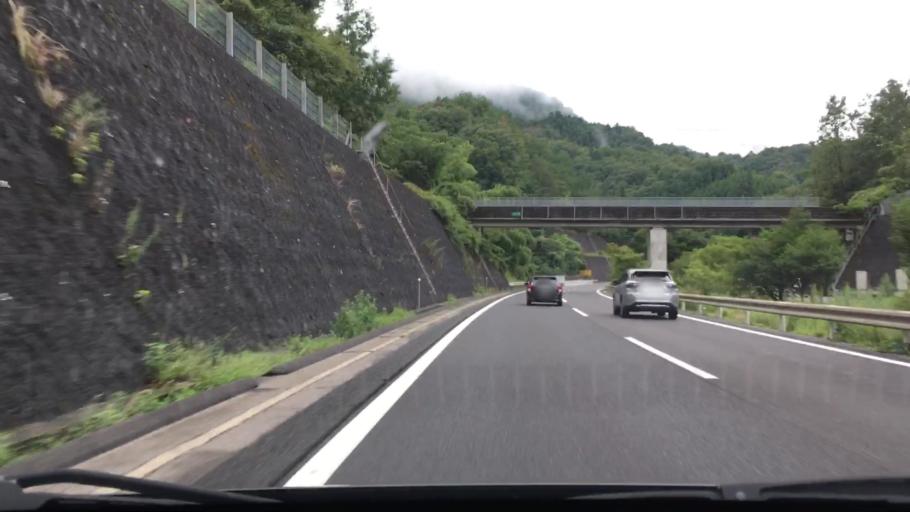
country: JP
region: Hiroshima
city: Hiroshima-shi
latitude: 34.5457
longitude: 132.4520
